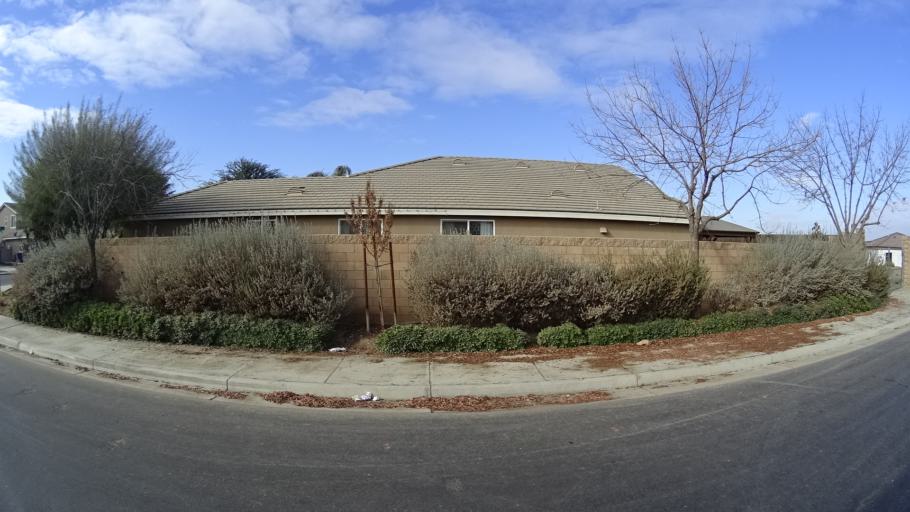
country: US
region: California
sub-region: Kern County
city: Rosedale
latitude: 35.2995
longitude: -119.1371
